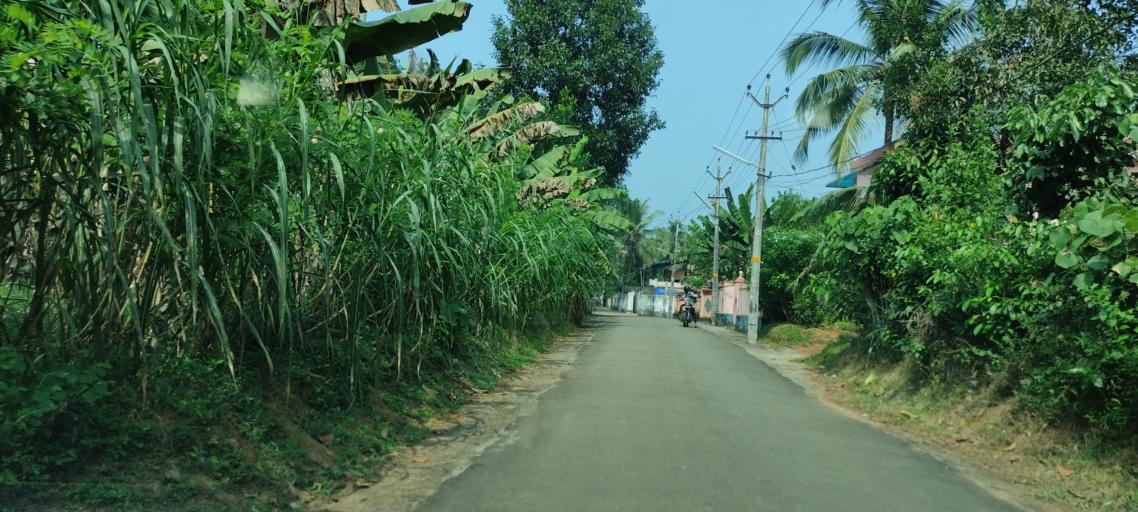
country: IN
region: Kerala
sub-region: Pattanamtitta
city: Adur
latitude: 9.2086
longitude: 76.6924
